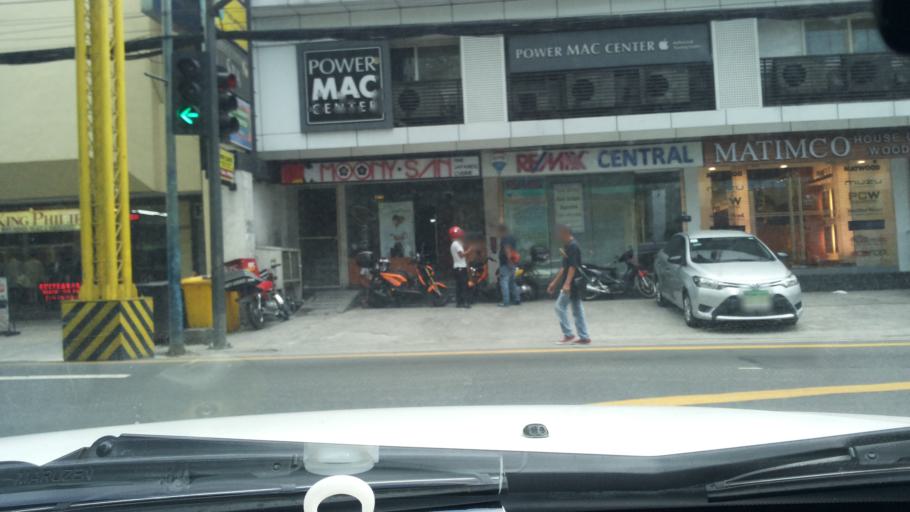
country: PH
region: Metro Manila
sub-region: Makati City
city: Makati City
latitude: 14.5503
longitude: 121.0234
